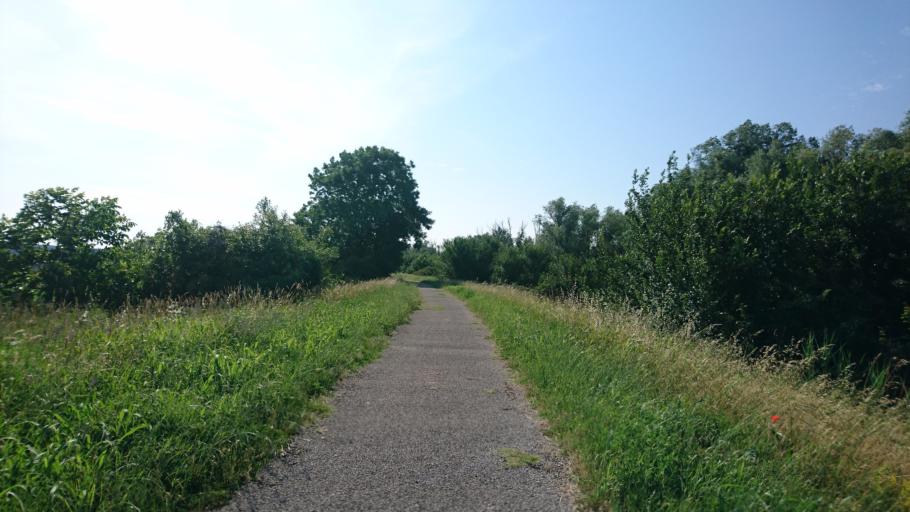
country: IT
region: Veneto
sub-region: Provincia di Verona
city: Villa Bartolomea
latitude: 45.1751
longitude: 11.3333
